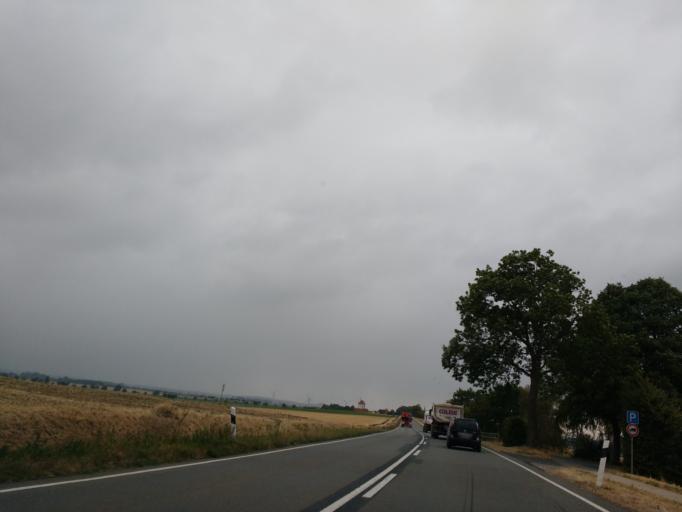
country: DE
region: Lower Saxony
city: Schellerten
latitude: 52.2016
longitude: 10.1615
